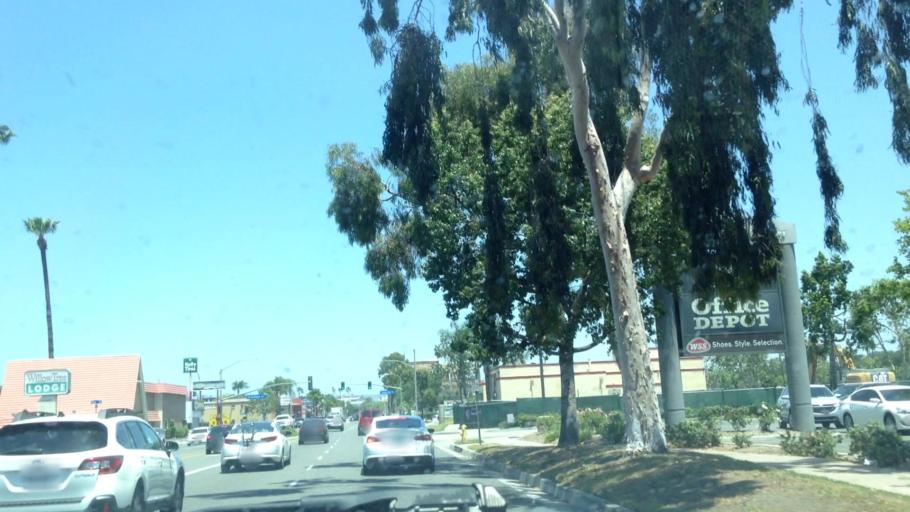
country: US
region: California
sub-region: Orange County
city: Fullerton
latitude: 33.8605
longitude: -117.9242
